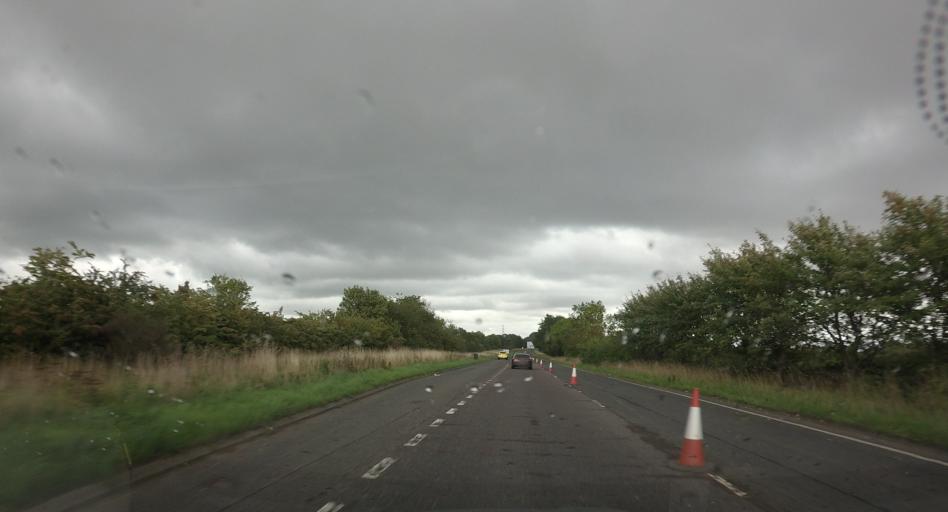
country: GB
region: Scotland
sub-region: Clackmannanshire
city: Clackmannan
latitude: 56.1026
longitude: -3.7265
